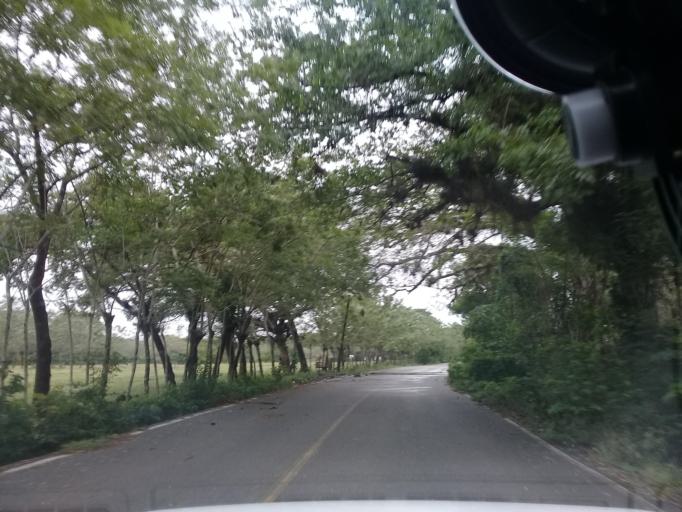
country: MX
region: Veracruz
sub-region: Chalma
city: San Pedro Coyutla
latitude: 21.2096
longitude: -98.4155
